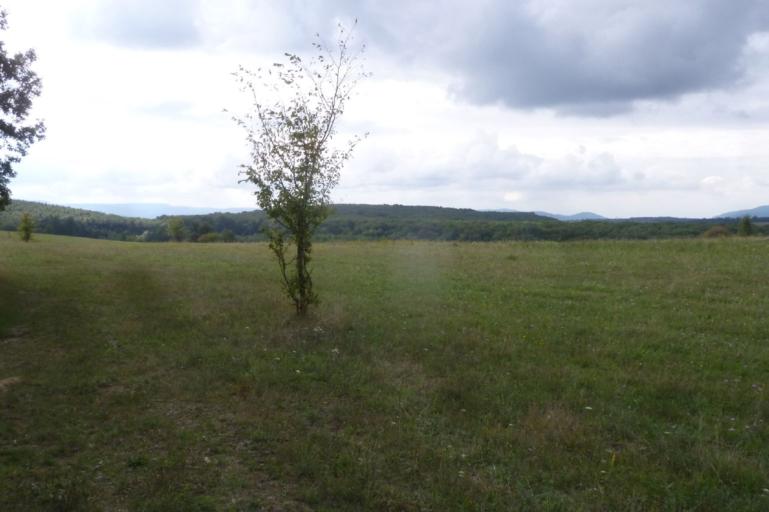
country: HU
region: Pest
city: Kismaros
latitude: 47.8534
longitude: 18.9666
